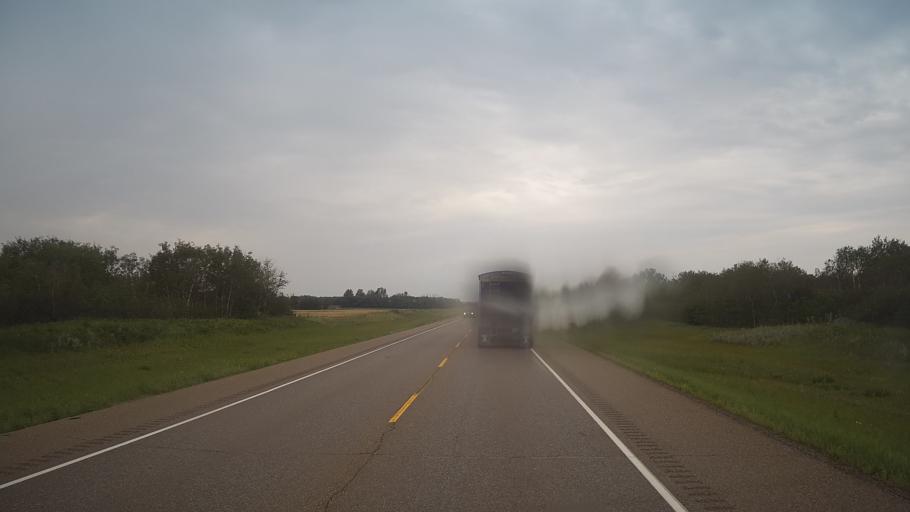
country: CA
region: Saskatchewan
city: Langham
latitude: 52.1294
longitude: -107.0574
